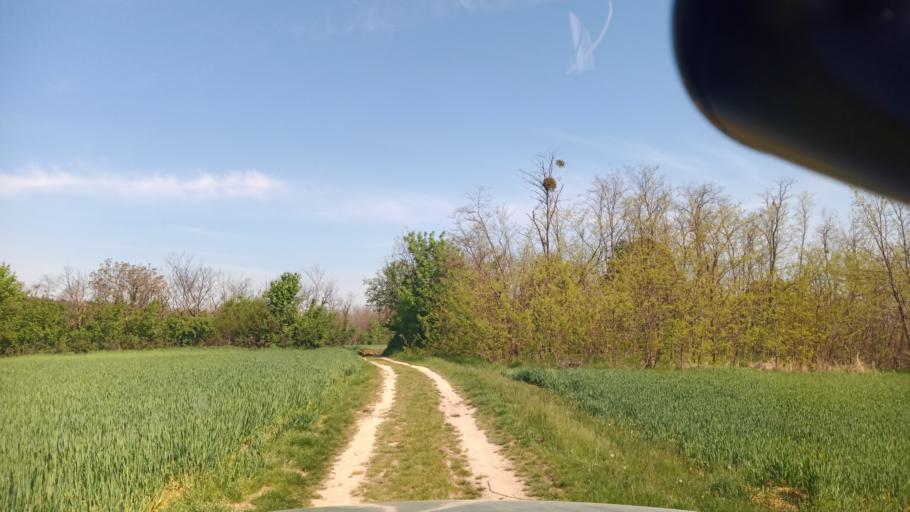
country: HU
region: Zala
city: Heviz
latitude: 46.7766
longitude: 17.0931
